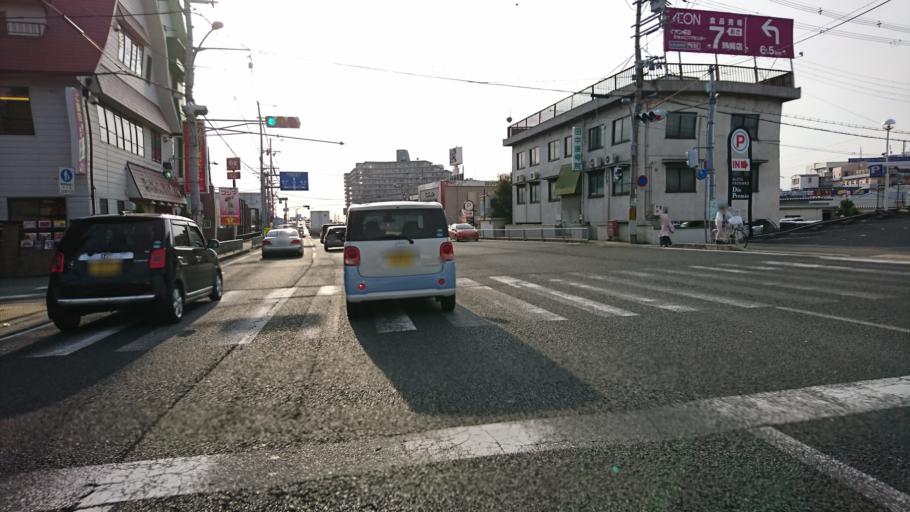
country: JP
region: Hyogo
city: Kakogawacho-honmachi
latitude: 34.7202
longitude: 134.8945
